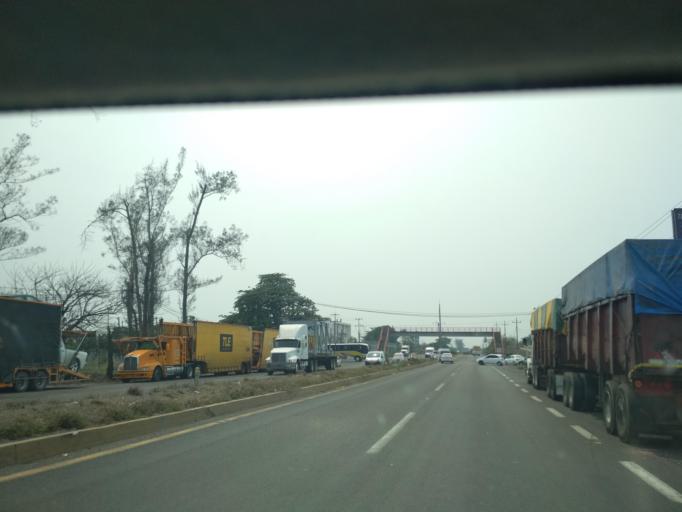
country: MX
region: Veracruz
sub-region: Veracruz
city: Delfino Victoria (Santa Fe)
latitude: 19.1834
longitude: -96.2603
